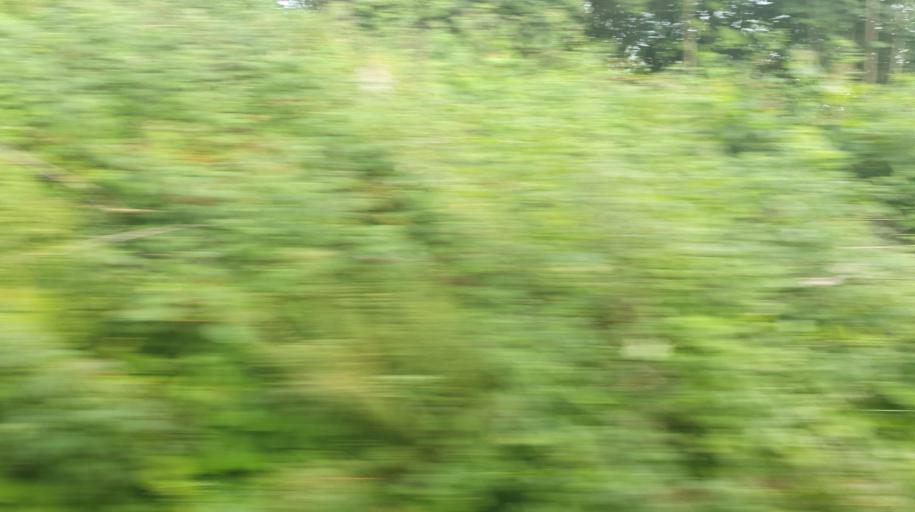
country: NO
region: Nord-Trondelag
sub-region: Levanger
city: Skogn
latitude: 63.7139
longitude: 11.2021
